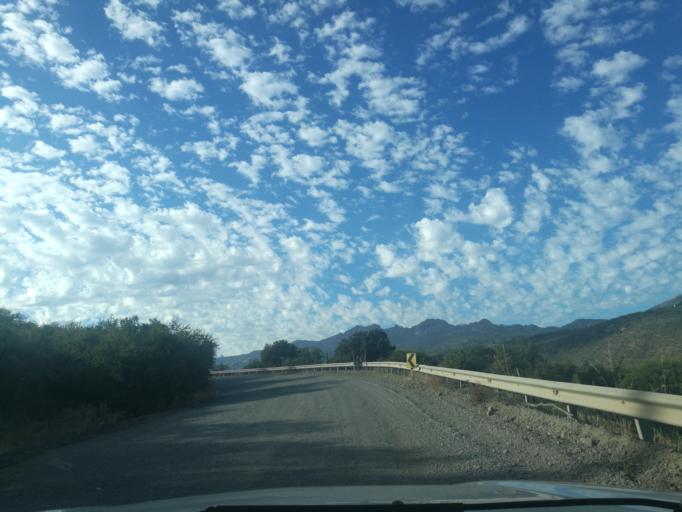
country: CL
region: O'Higgins
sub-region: Provincia de Cachapoal
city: Machali
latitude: -34.2459
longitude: -70.4692
